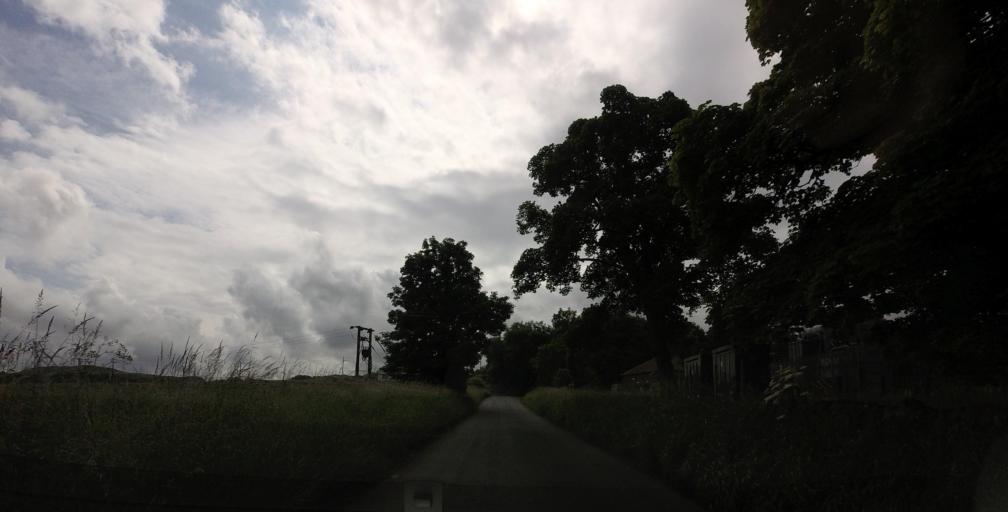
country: GB
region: Scotland
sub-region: West Lothian
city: Kirknewton
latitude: 55.8897
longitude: -3.4045
